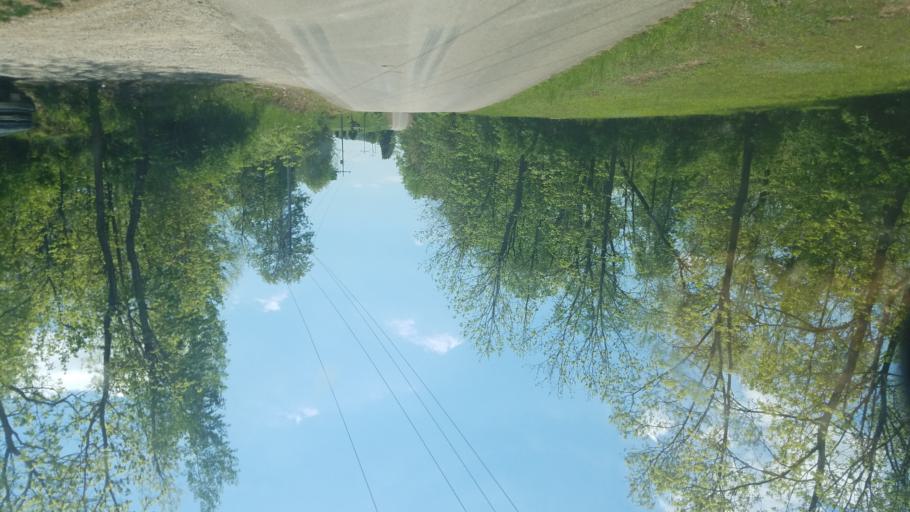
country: US
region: Ohio
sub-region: Knox County
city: Oak Hill
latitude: 40.2924
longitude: -82.2424
